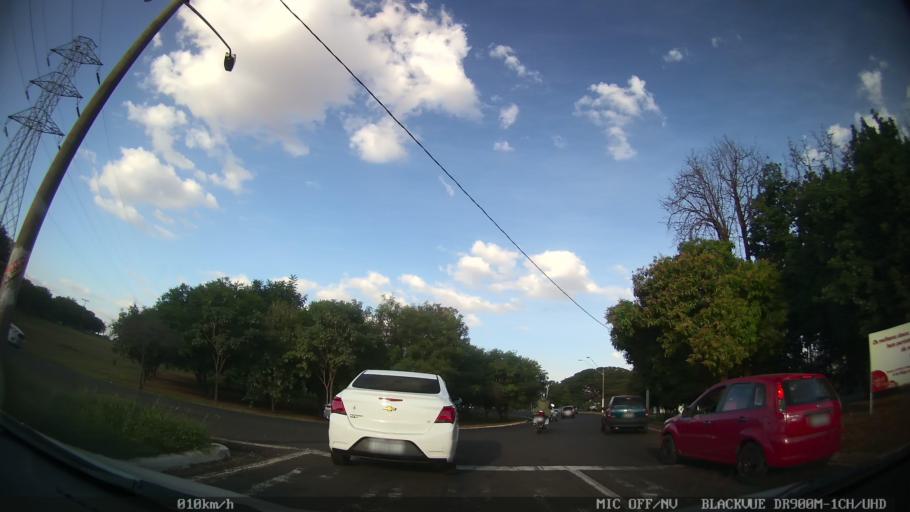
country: BR
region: Sao Paulo
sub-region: Ribeirao Preto
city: Ribeirao Preto
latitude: -21.1875
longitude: -47.7860
